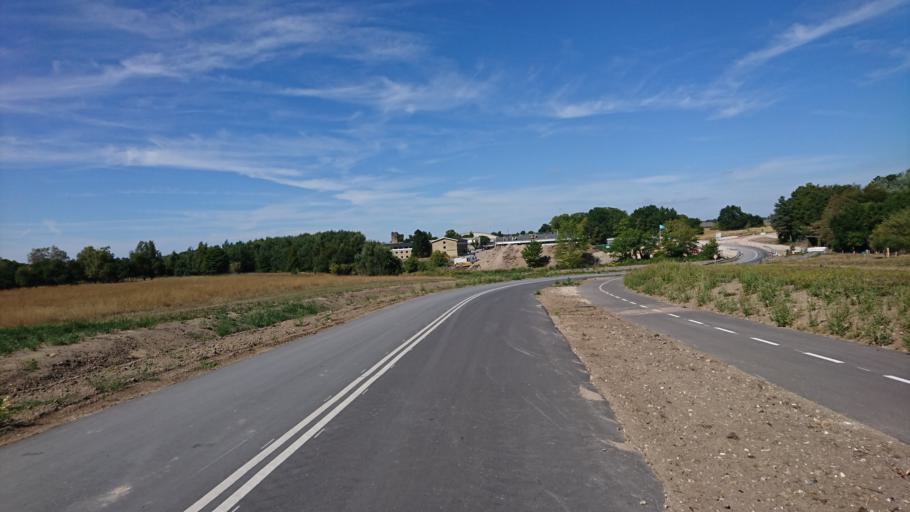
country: DK
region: Capital Region
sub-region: Ballerup Kommune
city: Malov
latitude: 55.7593
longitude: 12.3093
